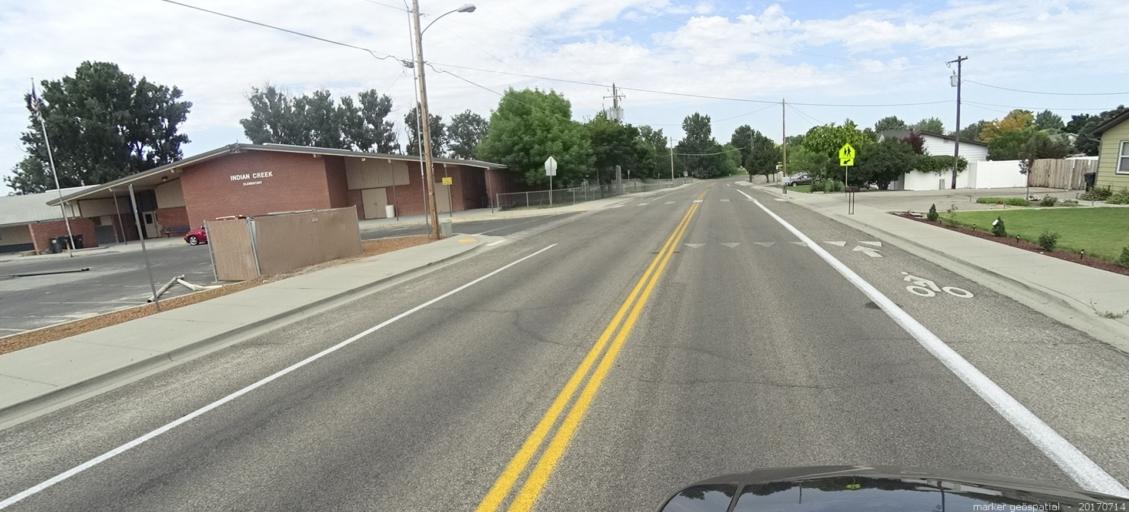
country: US
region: Idaho
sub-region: Ada County
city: Kuna
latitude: 43.4921
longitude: -116.4256
